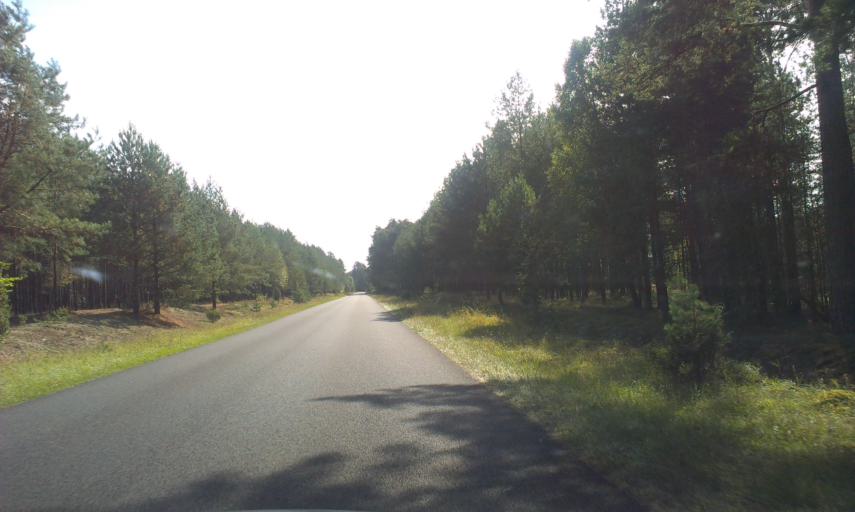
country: PL
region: Greater Poland Voivodeship
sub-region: Powiat zlotowski
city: Okonek
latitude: 53.5188
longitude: 16.9699
